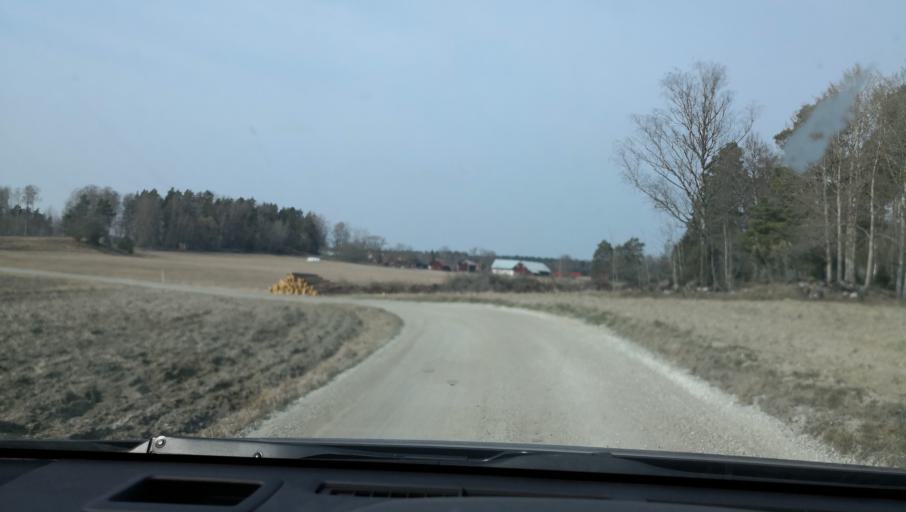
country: SE
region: OErebro
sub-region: Lindesbergs Kommun
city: Frovi
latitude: 59.3468
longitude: 15.4429
